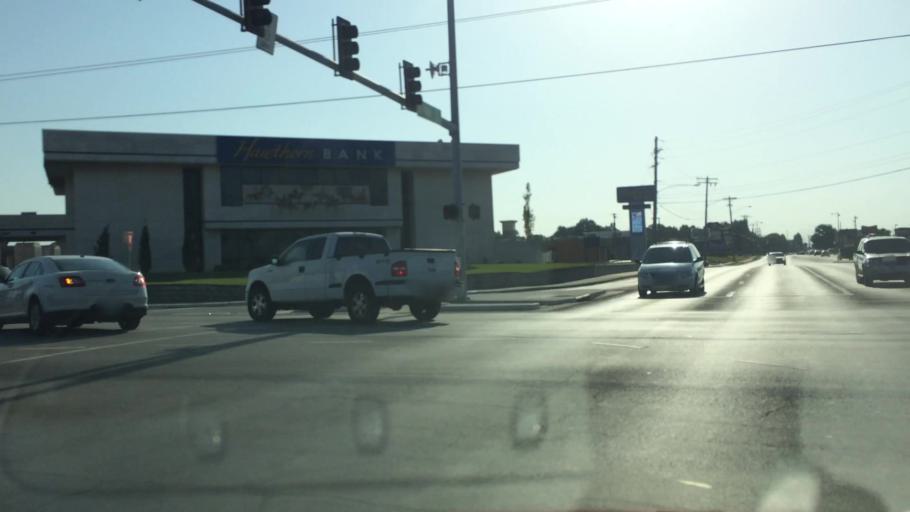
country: US
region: Missouri
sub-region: Greene County
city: Springfield
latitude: 37.1600
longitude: -93.2955
